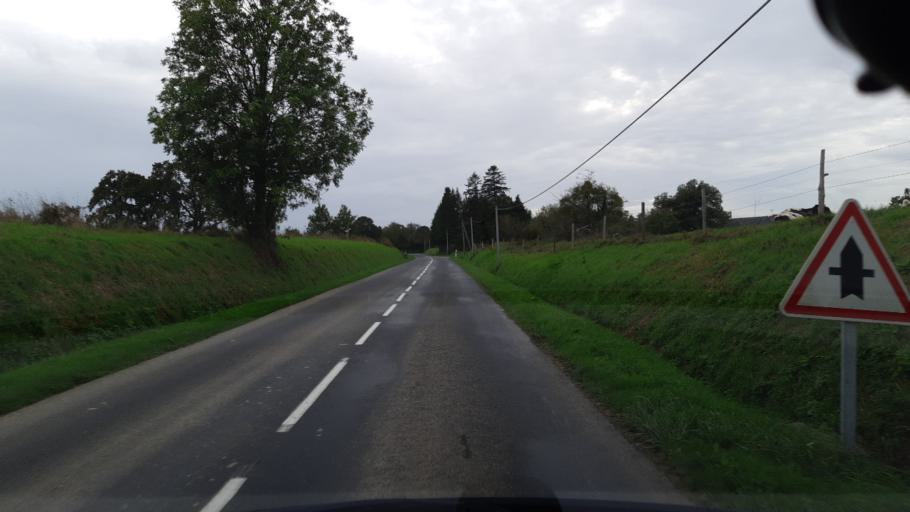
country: FR
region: Lower Normandy
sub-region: Departement de la Manche
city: Percy
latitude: 48.9972
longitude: -1.1975
